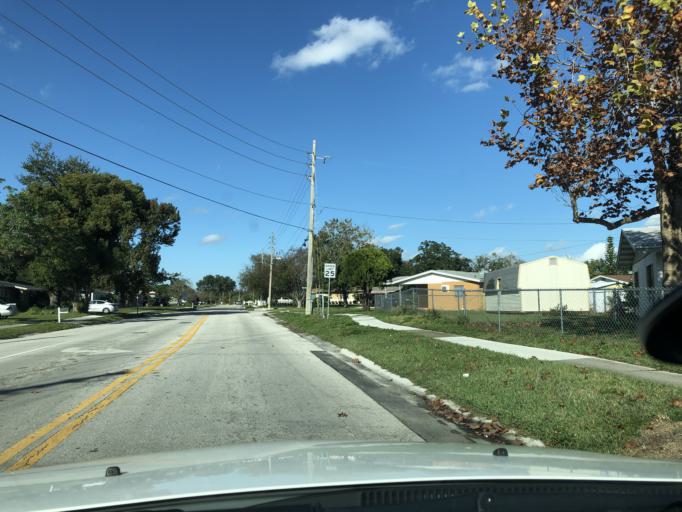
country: US
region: Florida
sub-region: Orange County
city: Oak Ridge
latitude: 28.4724
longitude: -81.4334
